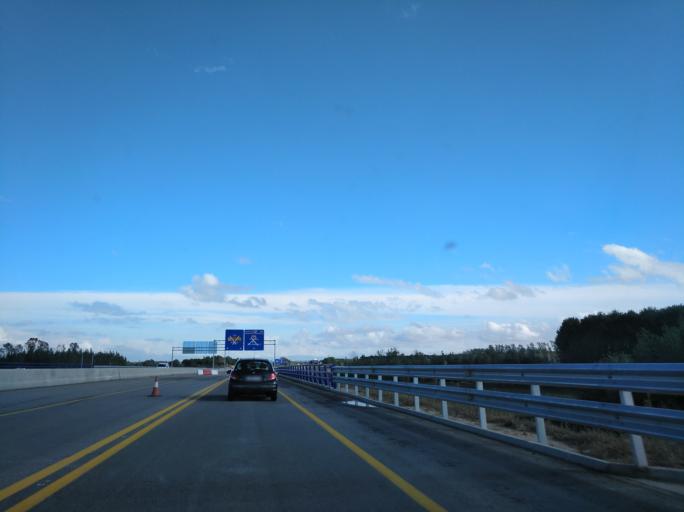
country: ES
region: Catalonia
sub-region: Provincia de Girona
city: Sils
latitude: 41.7916
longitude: 2.7577
